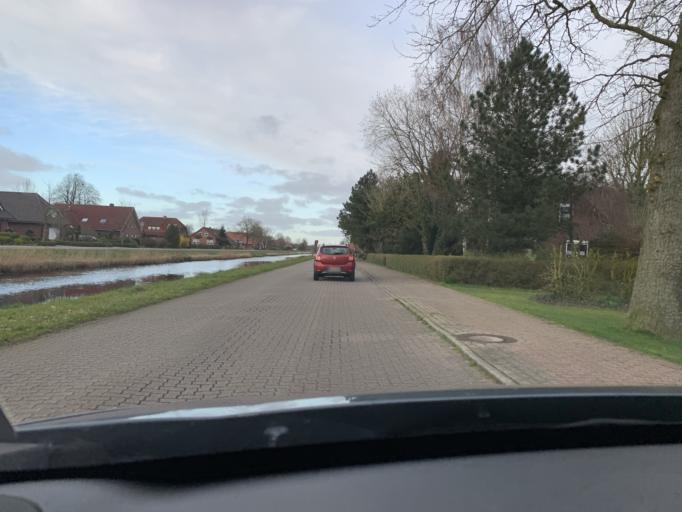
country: DE
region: Lower Saxony
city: Schwerinsdorf
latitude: 53.2744
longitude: 7.7016
